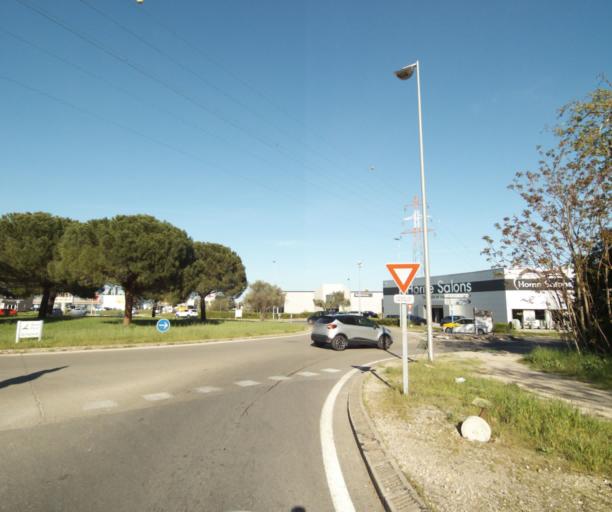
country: FR
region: Languedoc-Roussillon
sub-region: Departement de l'Herault
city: Lattes
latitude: 43.5816
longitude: 3.9211
